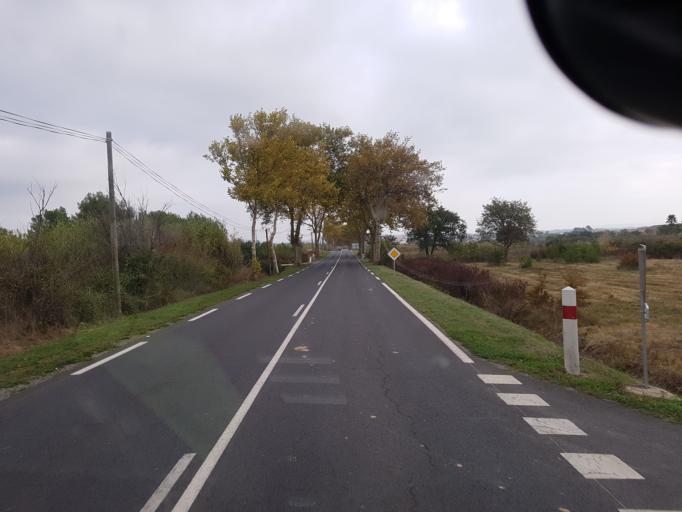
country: FR
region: Languedoc-Roussillon
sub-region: Departement de l'Herault
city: Meze
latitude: 43.4345
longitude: 3.5706
